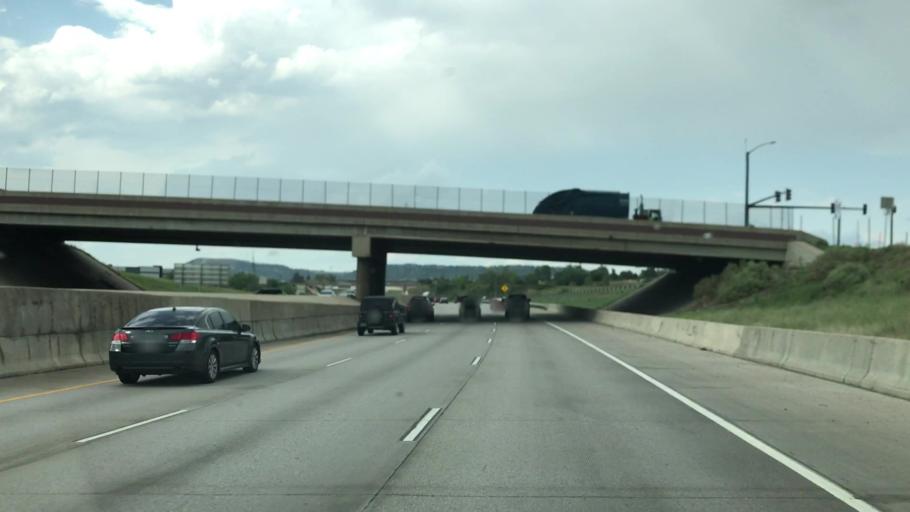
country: US
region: Colorado
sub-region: Douglas County
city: Castle Rock
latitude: 39.3795
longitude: -104.8607
